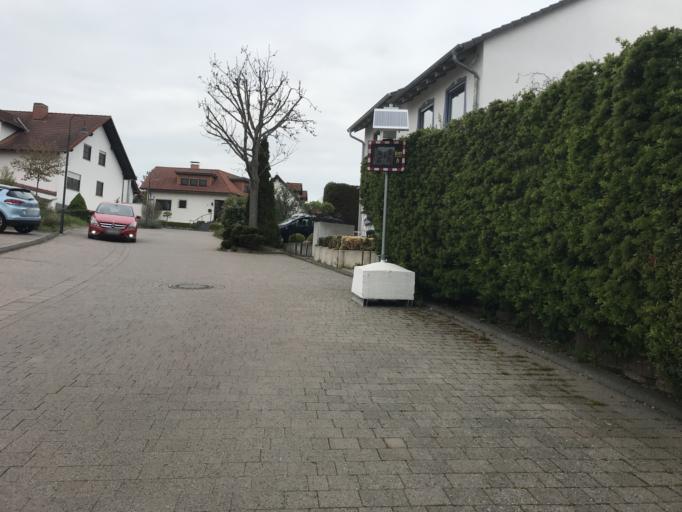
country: DE
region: Rheinland-Pfalz
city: Bubenheim
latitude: 49.9228
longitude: 8.0831
